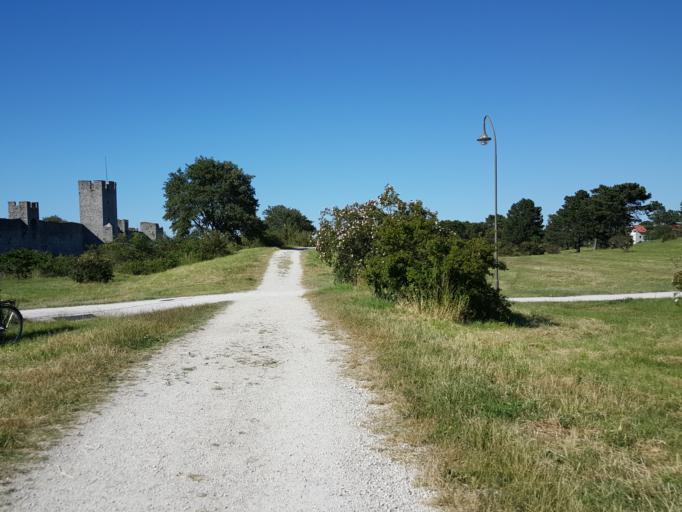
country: SE
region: Gotland
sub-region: Gotland
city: Visby
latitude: 57.6414
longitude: 18.3012
